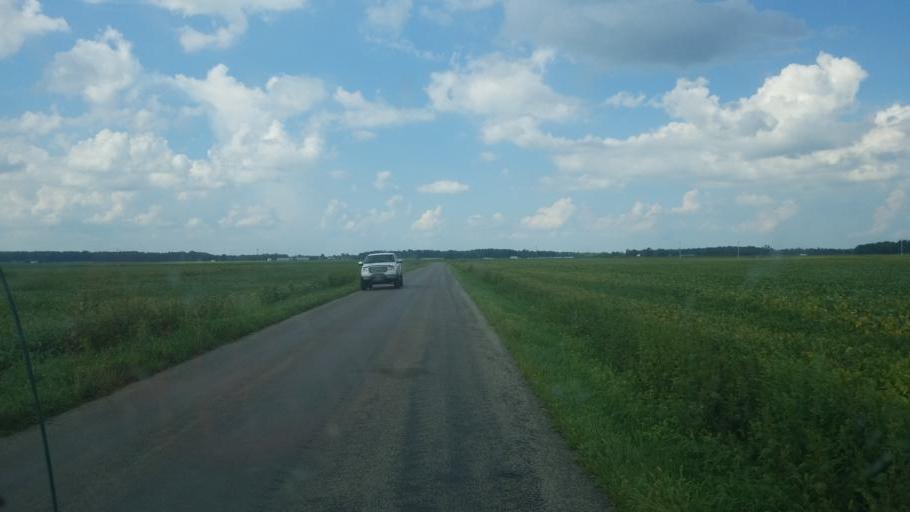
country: US
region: Ohio
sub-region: Huron County
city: Willard
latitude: 41.0151
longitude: -82.7092
